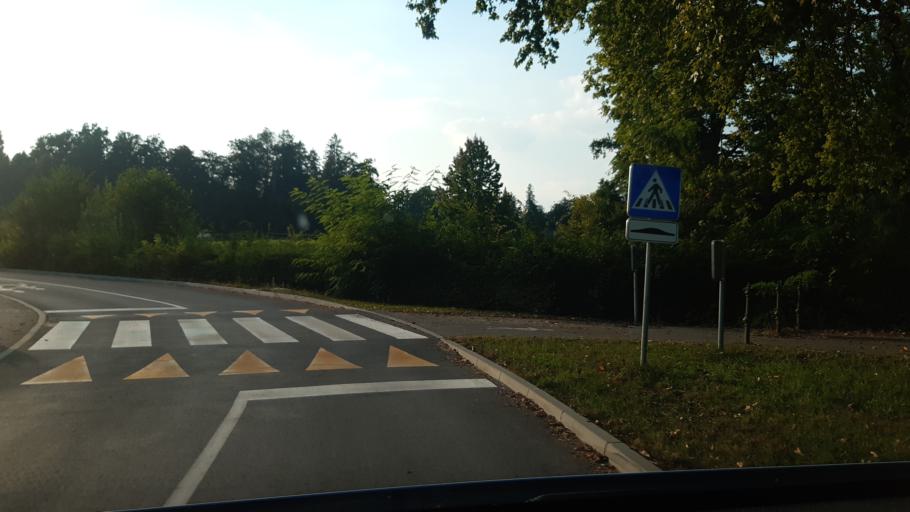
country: SI
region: Lukovica
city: Lukovica pri Domzalah
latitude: 46.1691
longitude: 14.6836
